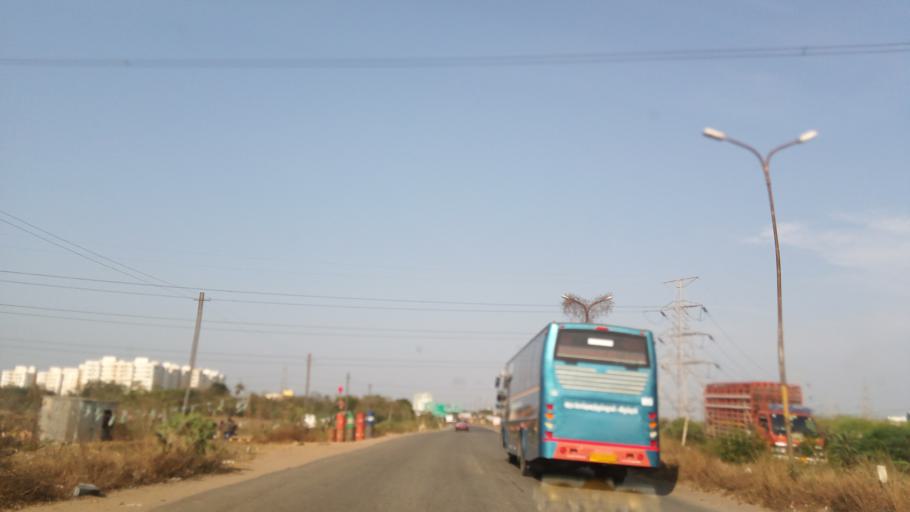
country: IN
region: Tamil Nadu
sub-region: Kancheepuram
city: Sriperumbudur
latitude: 12.9800
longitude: 79.9643
